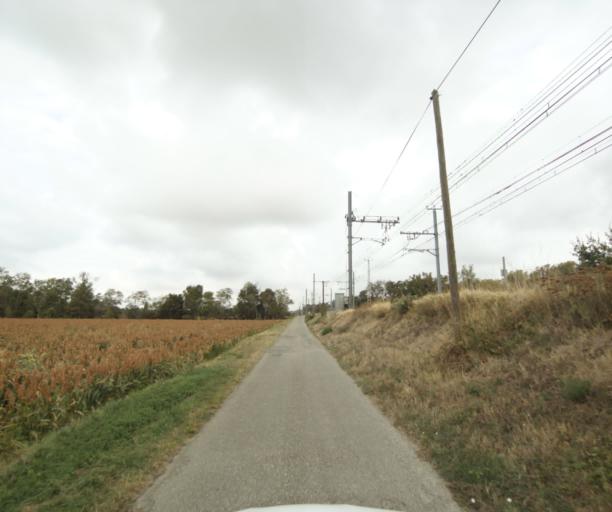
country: FR
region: Midi-Pyrenees
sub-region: Departement de la Haute-Garonne
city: Villefranche-de-Lauragais
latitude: 43.4016
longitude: 1.7115
